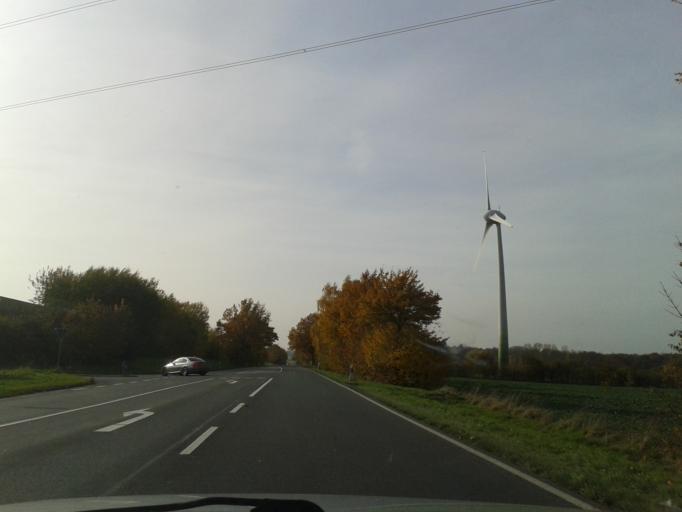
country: DE
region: North Rhine-Westphalia
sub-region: Regierungsbezirk Detmold
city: Buren
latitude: 51.5636
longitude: 8.5323
